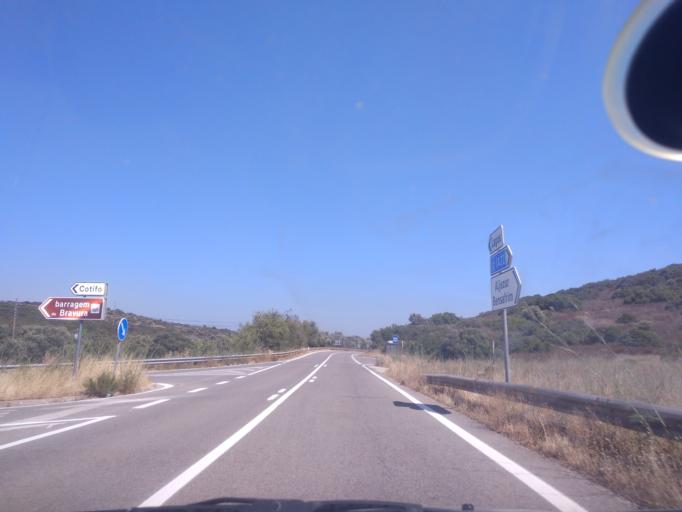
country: PT
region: Faro
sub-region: Lagos
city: Lagos
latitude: 37.1499
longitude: -8.7183
